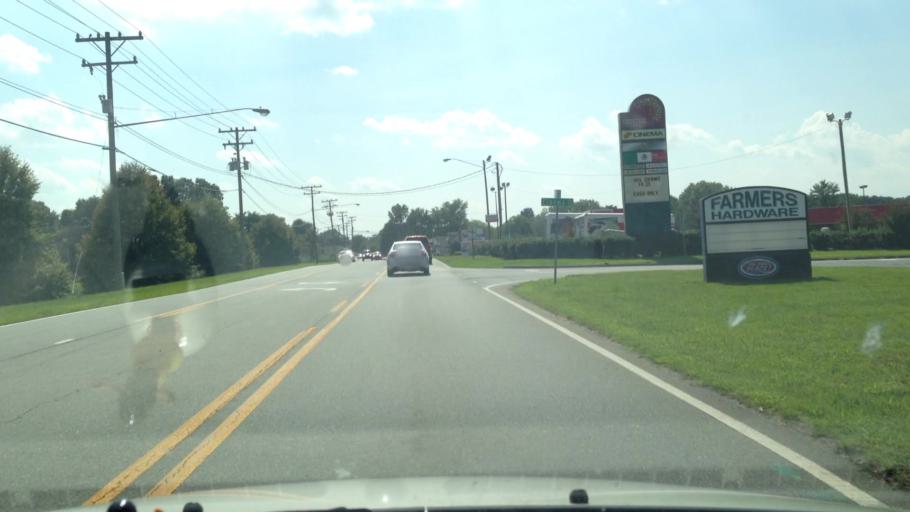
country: US
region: North Carolina
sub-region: Forsyth County
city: Kernersville
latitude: 36.1282
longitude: -80.0630
